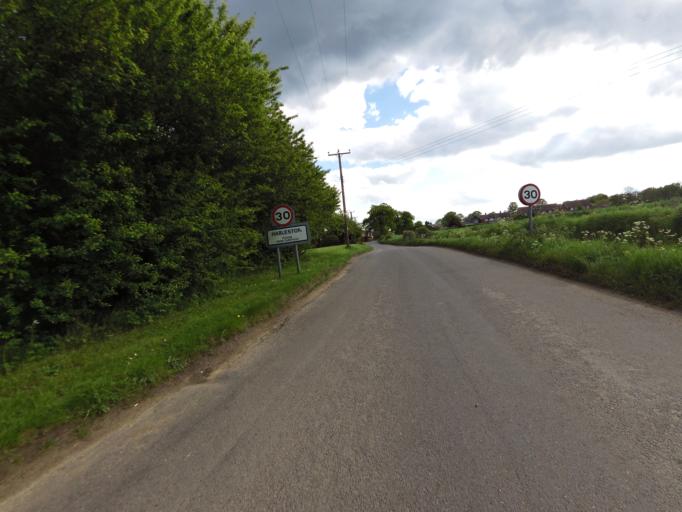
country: GB
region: England
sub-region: Suffolk
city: Elmswell
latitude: 52.2044
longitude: 0.9463
